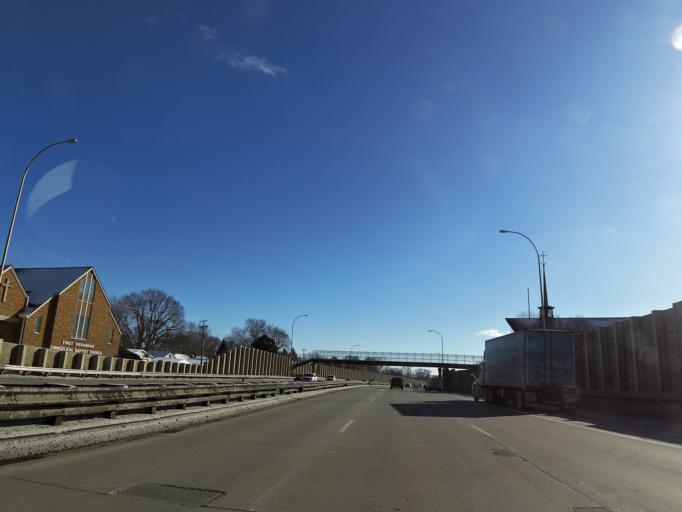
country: US
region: Minnesota
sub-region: Hennepin County
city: Saint Louis Park
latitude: 44.9278
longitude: -93.3499
